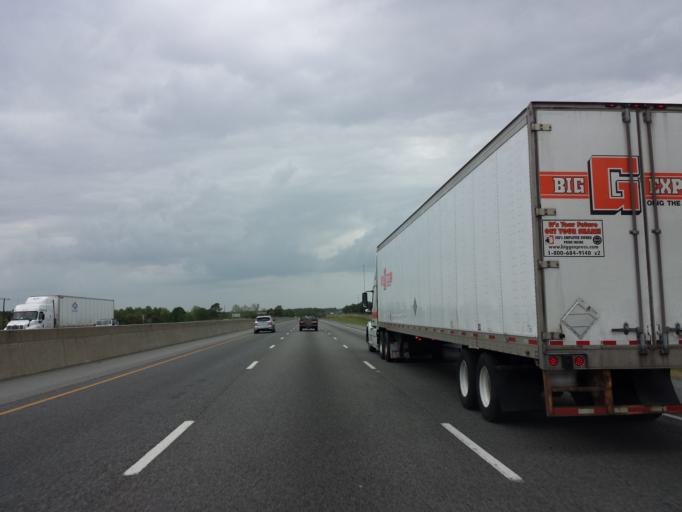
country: US
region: Georgia
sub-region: Tift County
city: Tifton
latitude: 31.5861
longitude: -83.5554
